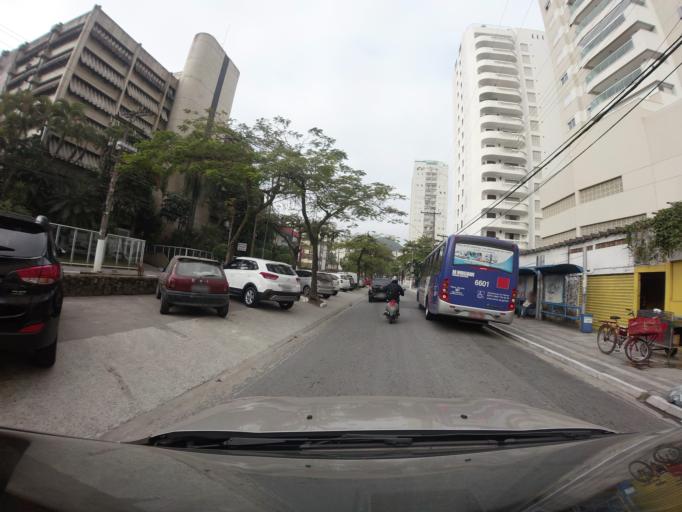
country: BR
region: Sao Paulo
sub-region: Guaruja
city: Guaruja
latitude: -23.9957
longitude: -46.2586
